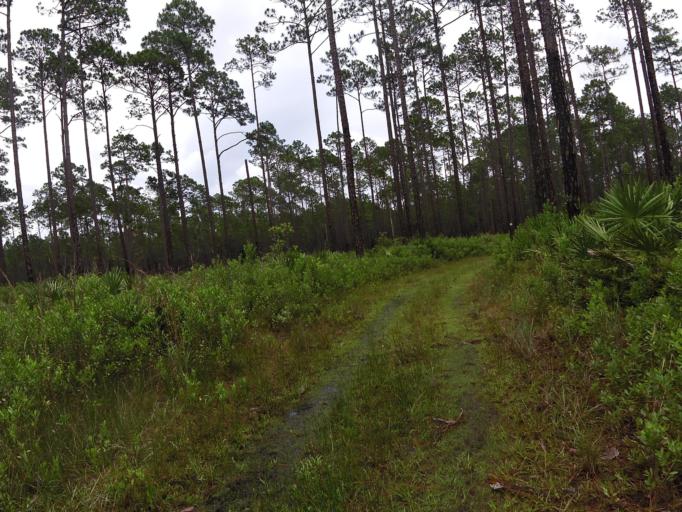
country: US
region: Florida
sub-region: Clay County
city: Green Cove Springs
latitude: 29.9651
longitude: -81.6301
